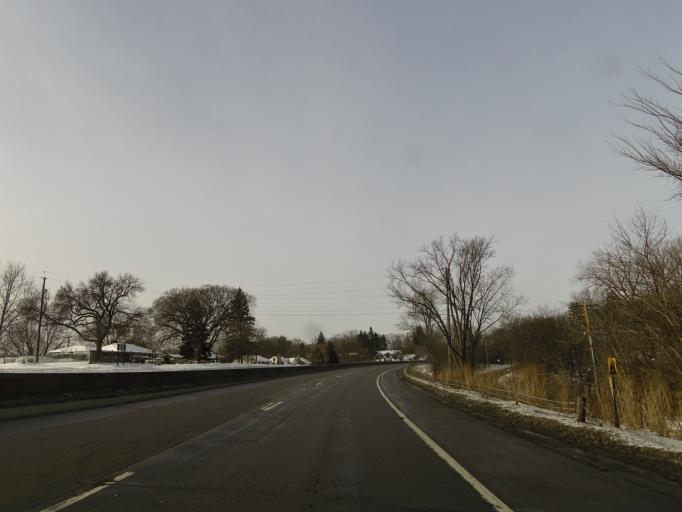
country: US
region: Minnesota
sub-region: Hennepin County
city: Minnetonka
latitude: 44.9106
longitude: -93.5125
